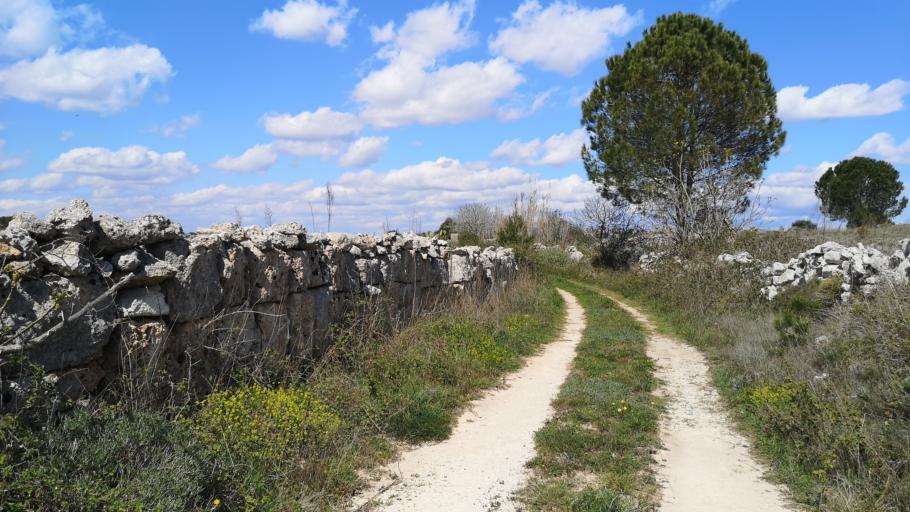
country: IT
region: Apulia
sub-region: Provincia di Lecce
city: Spongano
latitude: 40.0283
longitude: 18.3623
